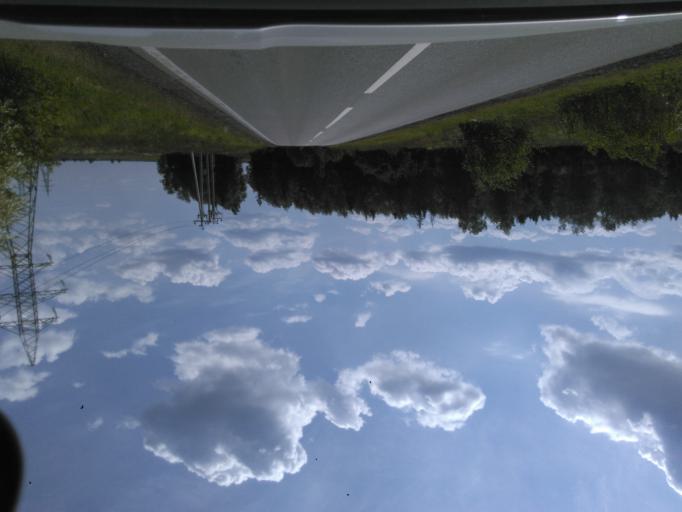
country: RU
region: Moskovskaya
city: Solnechnogorsk
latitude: 56.1427
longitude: 36.9777
